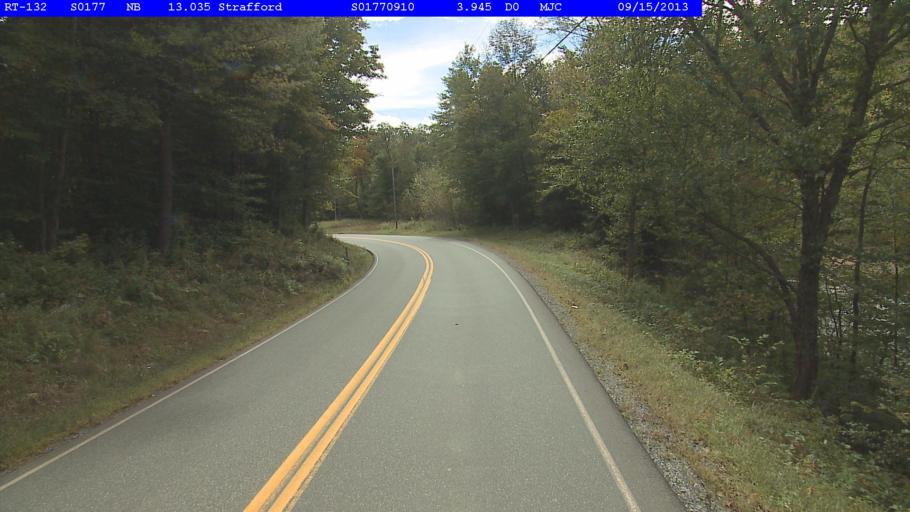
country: US
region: New Hampshire
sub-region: Grafton County
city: Hanover
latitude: 43.8357
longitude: -72.3342
